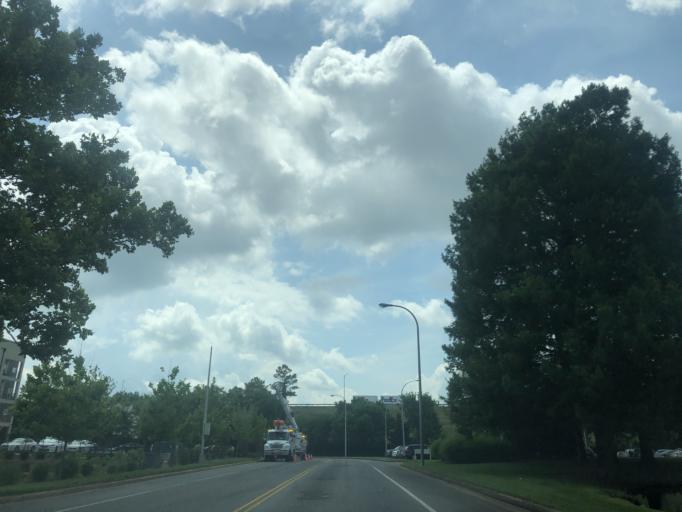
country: US
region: Tennessee
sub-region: Davidson County
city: Nashville
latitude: 36.1925
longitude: -86.7905
